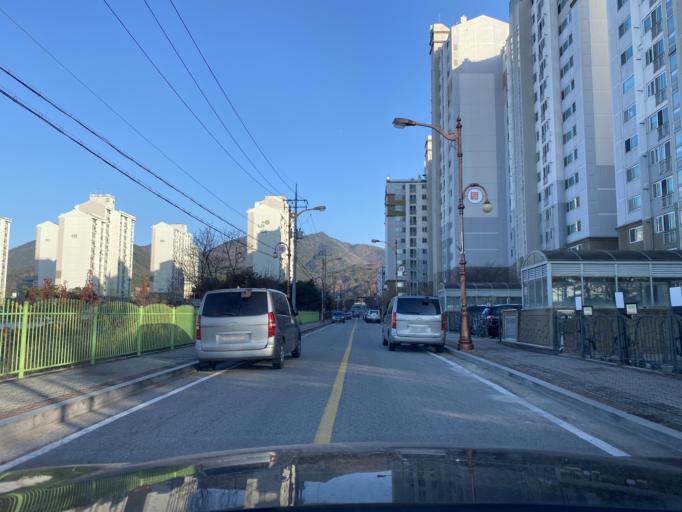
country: KR
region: Chungcheongnam-do
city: Yesan
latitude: 36.6966
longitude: 126.8316
